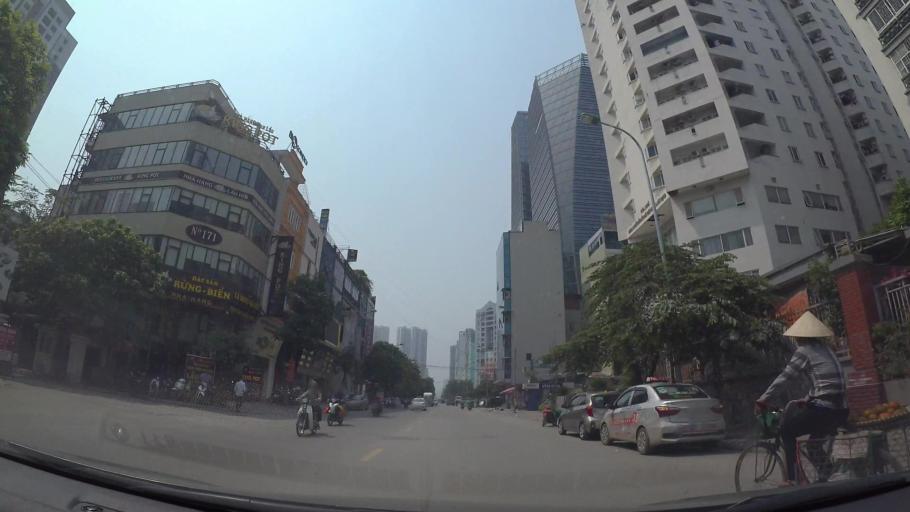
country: VN
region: Ha Noi
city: Thanh Xuan
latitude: 21.0008
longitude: 105.8015
